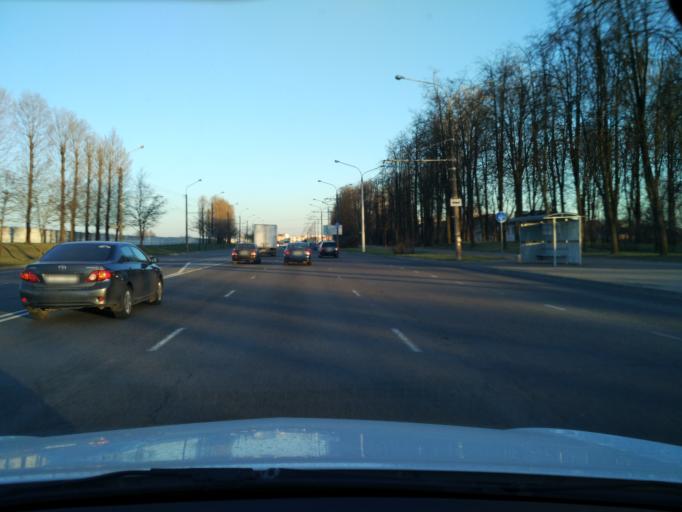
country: BY
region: Minsk
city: Syenitsa
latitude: 53.8651
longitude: 27.5299
